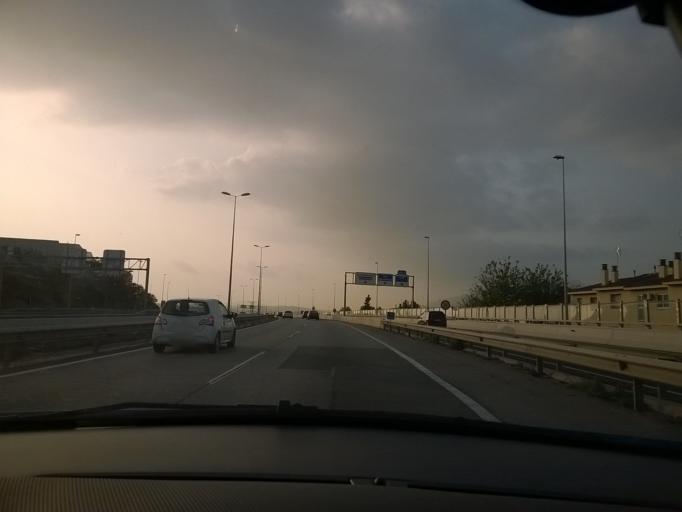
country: ES
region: Catalonia
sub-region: Provincia de Barcelona
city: Abrera
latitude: 41.5211
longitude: 1.8936
